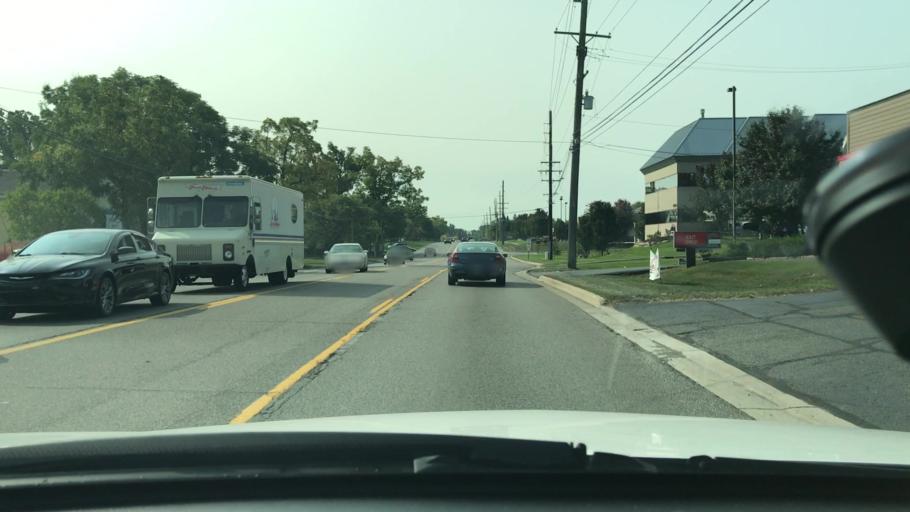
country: US
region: Michigan
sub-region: Oakland County
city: Wolverine Lake
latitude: 42.5975
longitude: -83.4463
